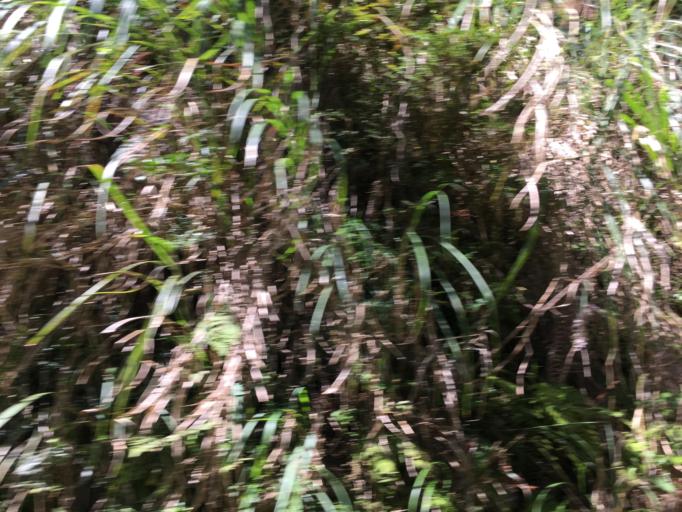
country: TW
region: Taiwan
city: Daxi
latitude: 24.5524
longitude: 121.3965
